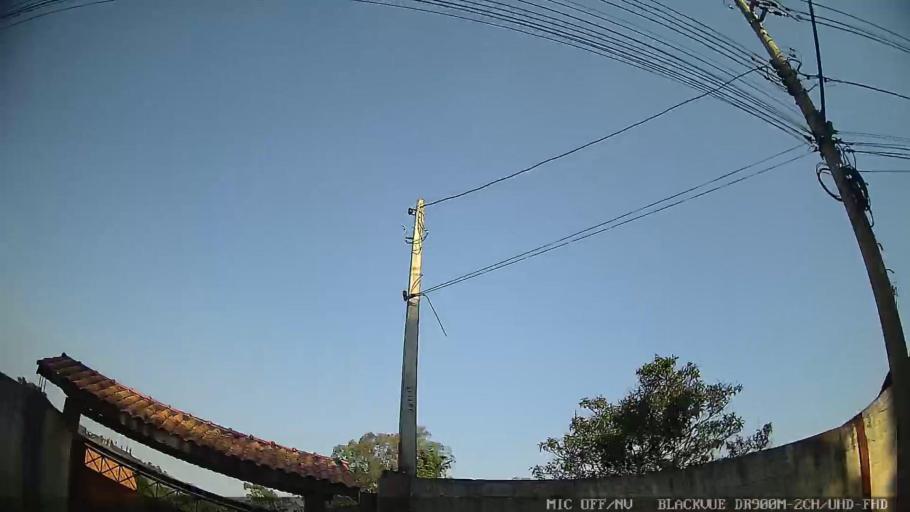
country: BR
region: Sao Paulo
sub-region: Itatiba
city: Itatiba
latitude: -22.9859
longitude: -46.8307
